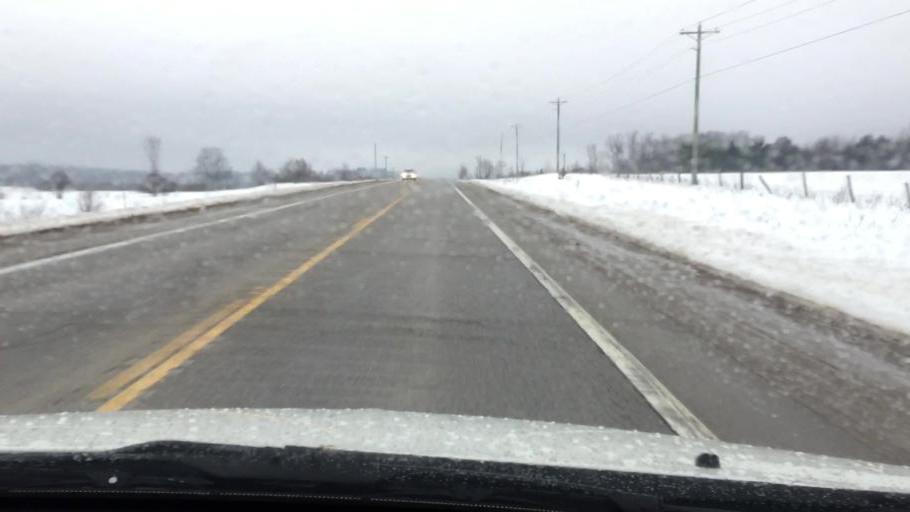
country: US
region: Michigan
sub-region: Charlevoix County
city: East Jordan
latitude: 45.1267
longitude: -85.1355
